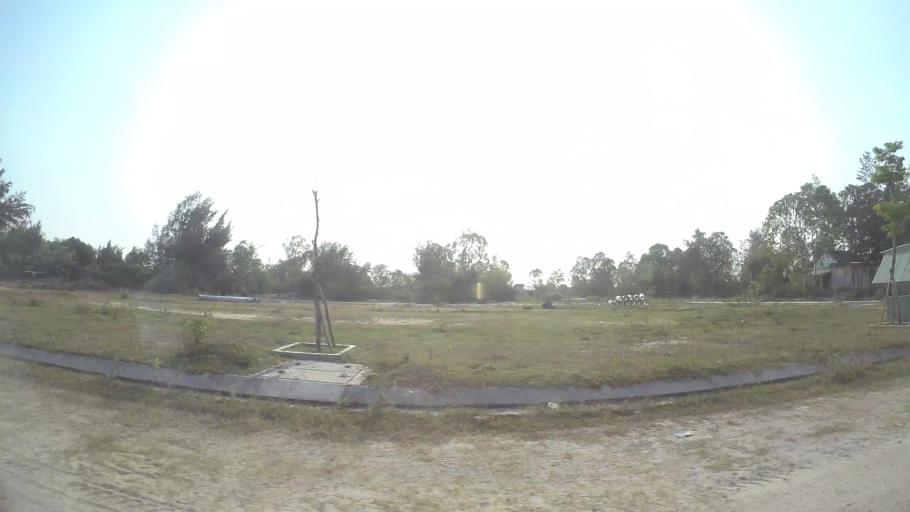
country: VN
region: Da Nang
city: Ngu Hanh Son
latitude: 15.9623
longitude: 108.2647
